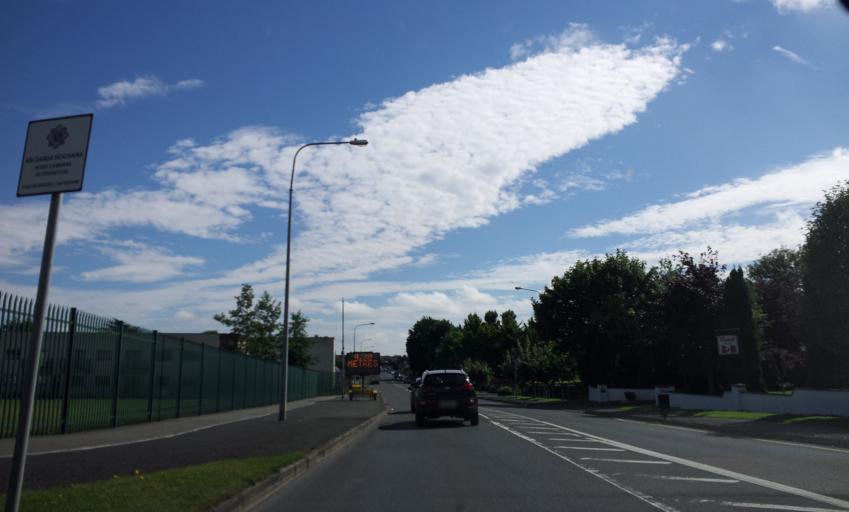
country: IE
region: Leinster
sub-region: Laois
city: Portlaoise
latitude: 53.0340
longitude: -7.3135
